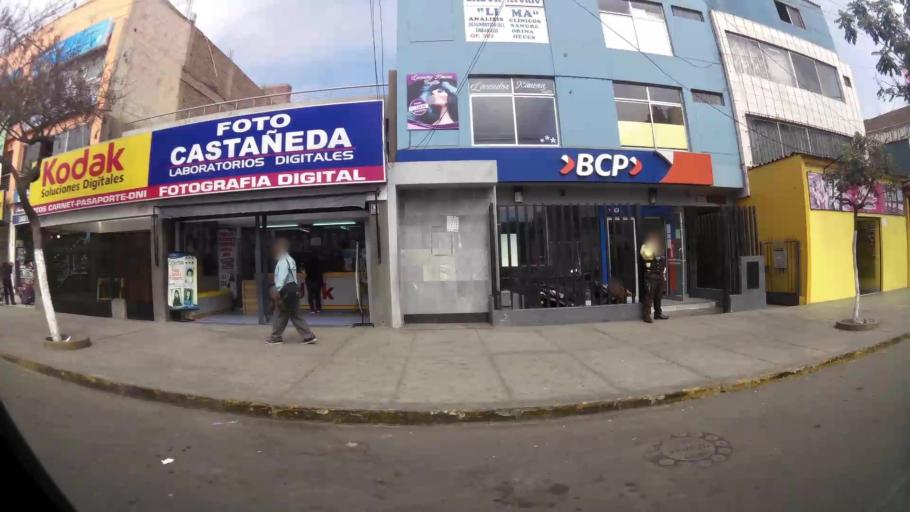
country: PE
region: La Libertad
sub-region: Provincia de Trujillo
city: Trujillo
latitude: -8.1143
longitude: -79.0243
